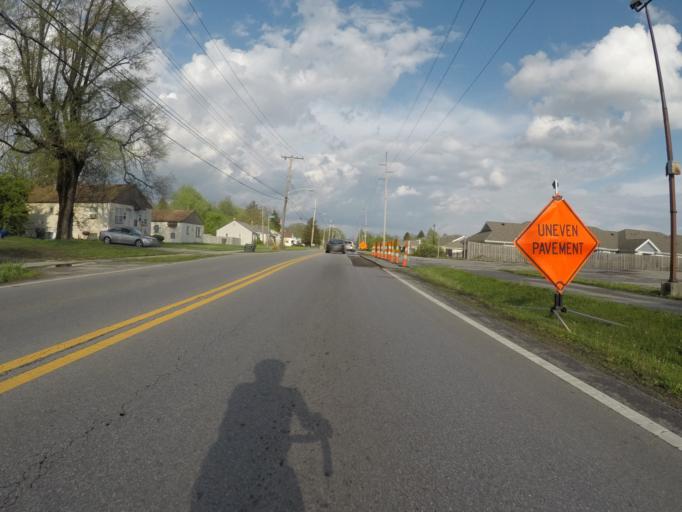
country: US
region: Ohio
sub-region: Franklin County
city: Bexley
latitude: 40.0133
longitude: -82.9595
